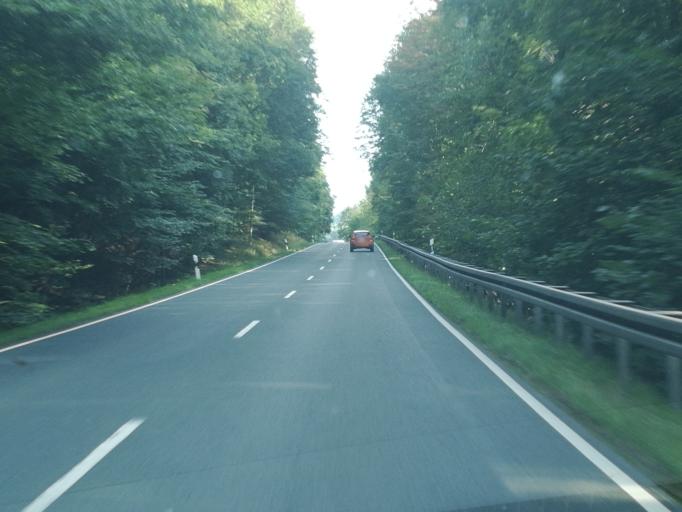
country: DE
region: Saxony
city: Adorf
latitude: 50.3352
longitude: 12.2509
